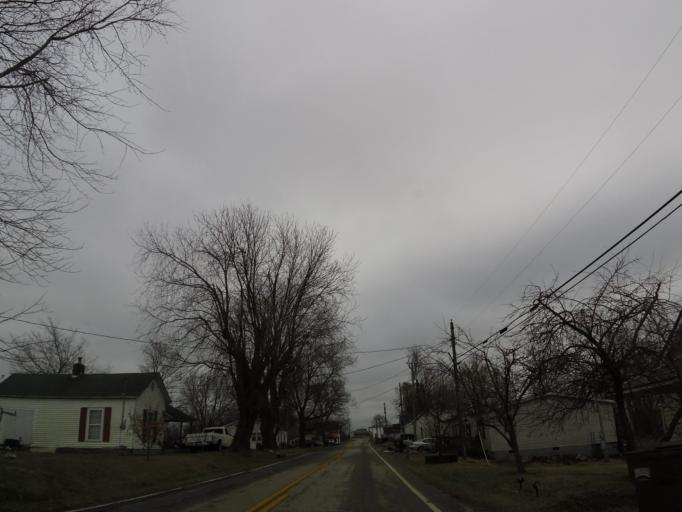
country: US
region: Kentucky
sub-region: Henry County
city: Eminence
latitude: 38.3431
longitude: -85.0564
